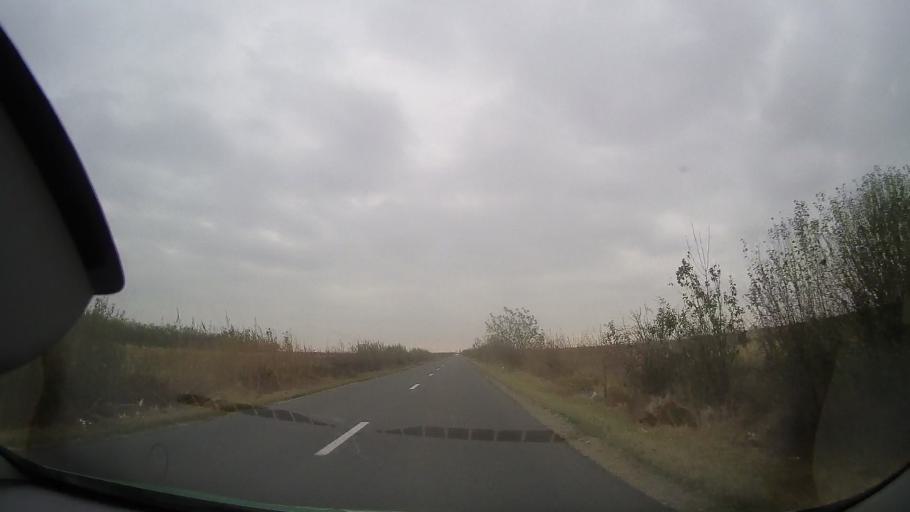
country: RO
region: Ialomita
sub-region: Comuna Manasia
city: Manasia
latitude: 44.7317
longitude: 26.6991
